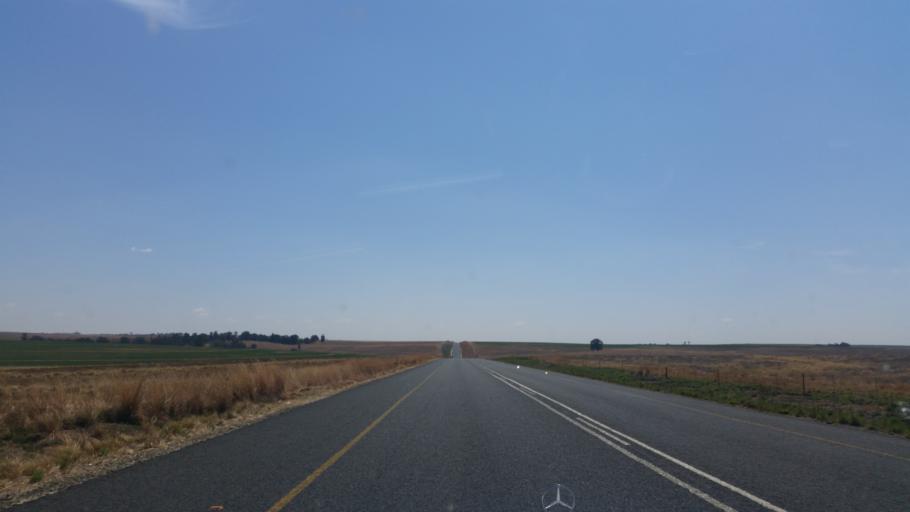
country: ZA
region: Orange Free State
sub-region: Thabo Mofutsanyana District Municipality
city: Phuthaditjhaba
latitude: -28.1844
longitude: 28.6857
